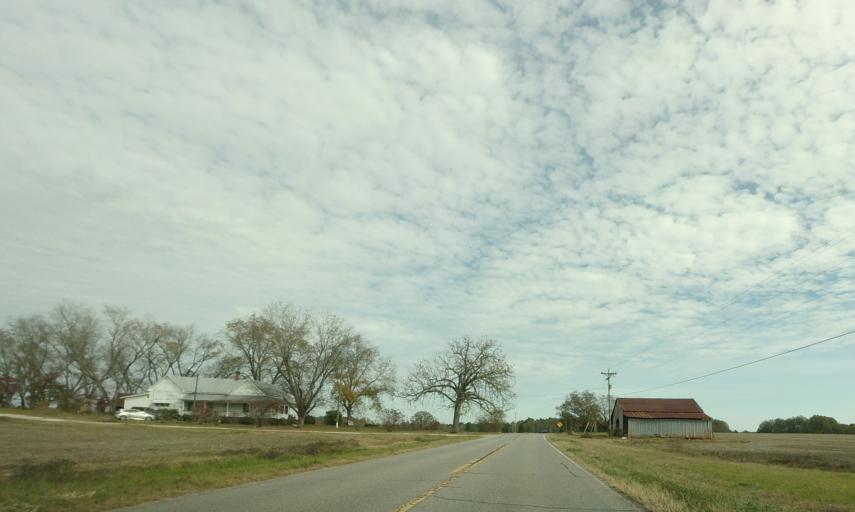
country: US
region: Georgia
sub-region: Bleckley County
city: Cochran
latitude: 32.3966
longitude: -83.2704
